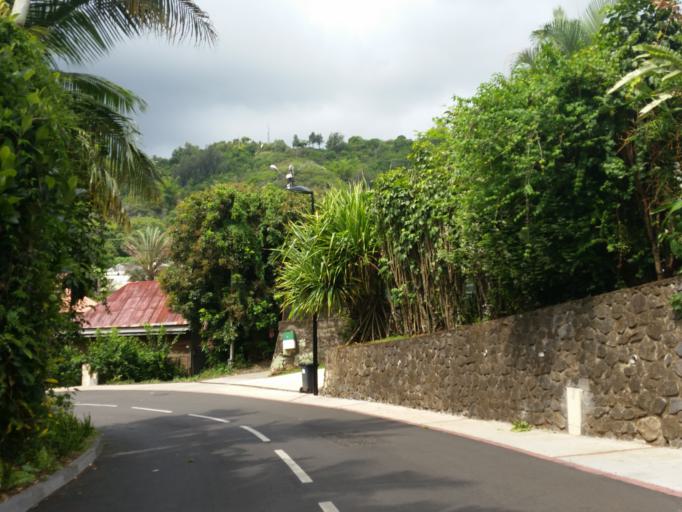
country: RE
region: Reunion
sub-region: Reunion
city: L'Entre-Deux
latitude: -21.2510
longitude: 55.4730
